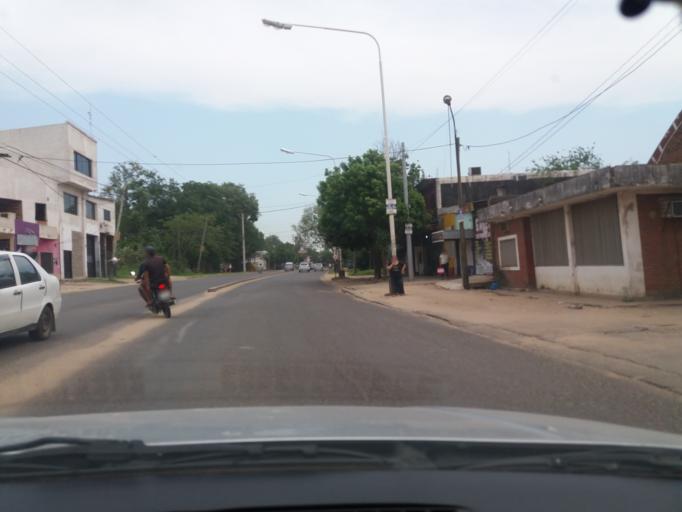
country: AR
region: Corrientes
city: Corrientes
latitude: -27.5118
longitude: -58.8093
